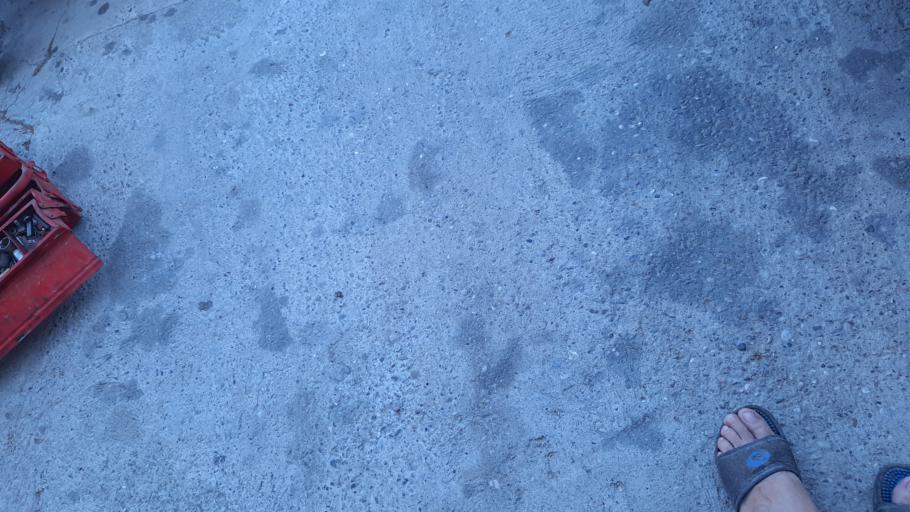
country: RS
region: Autonomna Pokrajina Vojvodina
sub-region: Juznobacki Okrug
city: Beocin
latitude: 45.2112
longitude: 19.7223
